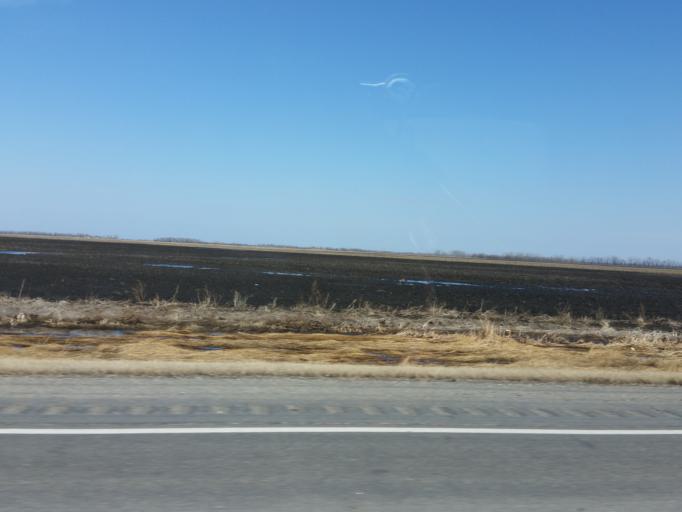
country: US
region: North Dakota
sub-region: Grand Forks County
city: Grand Forks Air Force Base
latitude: 48.1875
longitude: -97.3190
